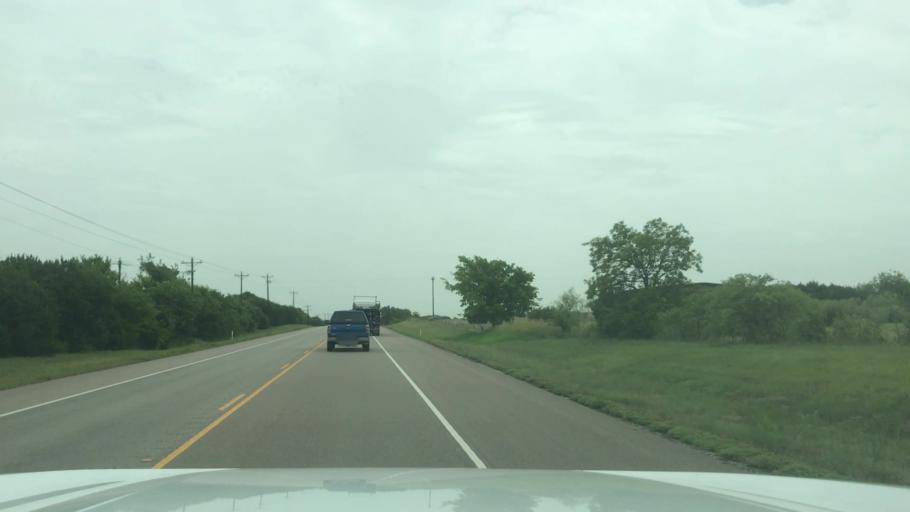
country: US
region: Texas
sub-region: Bosque County
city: Meridian
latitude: 31.9345
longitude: -97.6999
